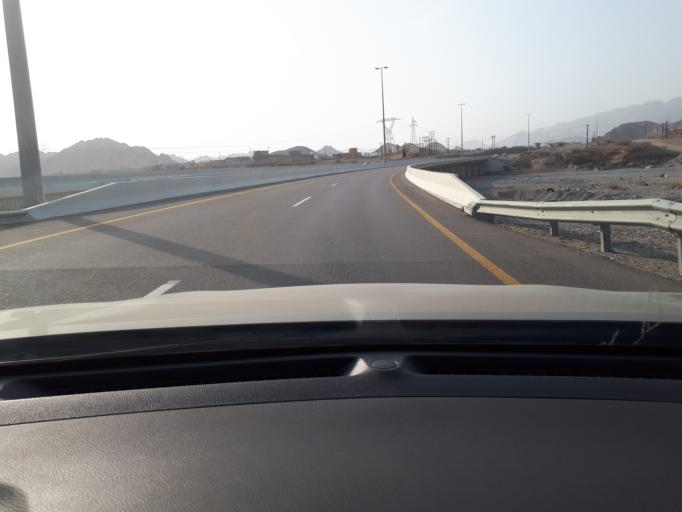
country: OM
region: Muhafazat Masqat
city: Muscat
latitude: 23.2656
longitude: 58.7578
